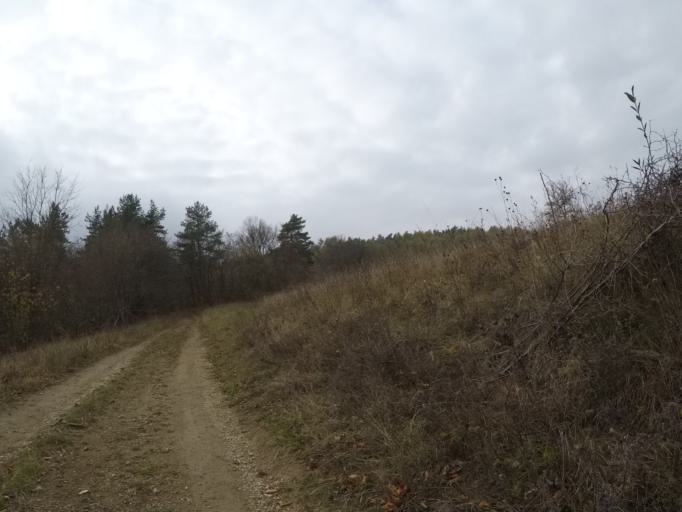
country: SK
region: Presovsky
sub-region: Okres Presov
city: Presov
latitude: 48.9031
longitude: 21.1722
